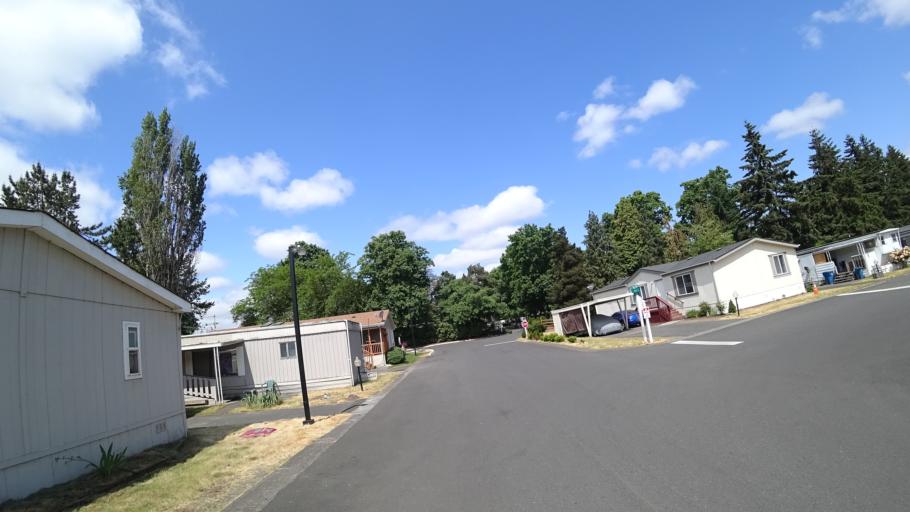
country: US
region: Washington
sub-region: Clark County
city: Vancouver
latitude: 45.6173
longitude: -122.6887
